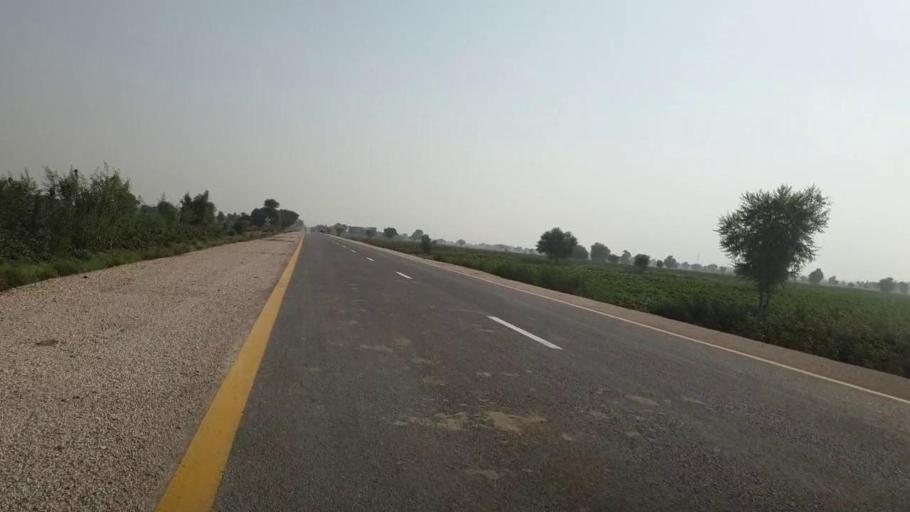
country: PK
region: Sindh
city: Bhan
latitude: 26.5439
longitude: 67.7872
